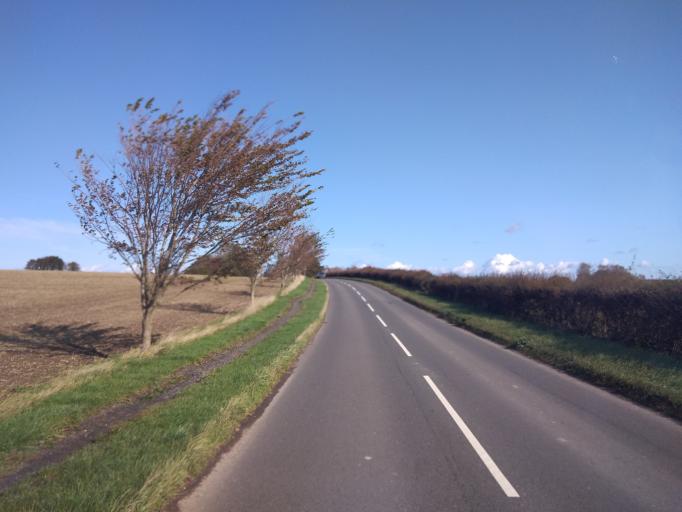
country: GB
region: England
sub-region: East Sussex
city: Seaford
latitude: 50.8170
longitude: 0.1619
